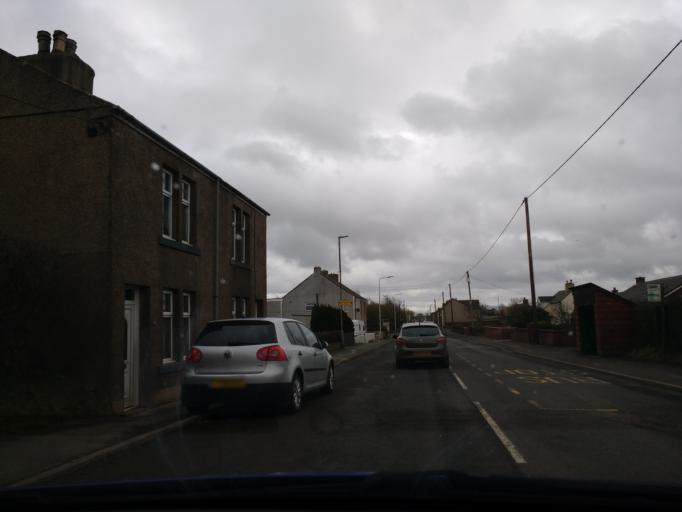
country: GB
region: England
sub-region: Cumbria
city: Dearham
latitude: 54.7042
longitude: -3.4513
